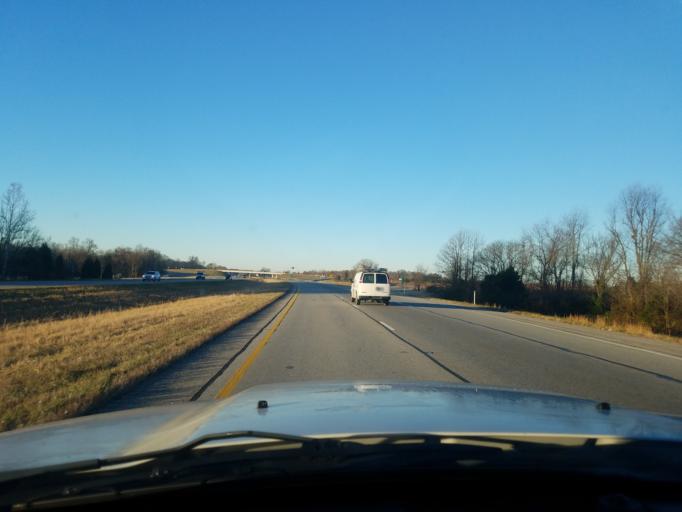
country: US
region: Indiana
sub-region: Floyd County
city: Georgetown
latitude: 38.2675
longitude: -85.9957
